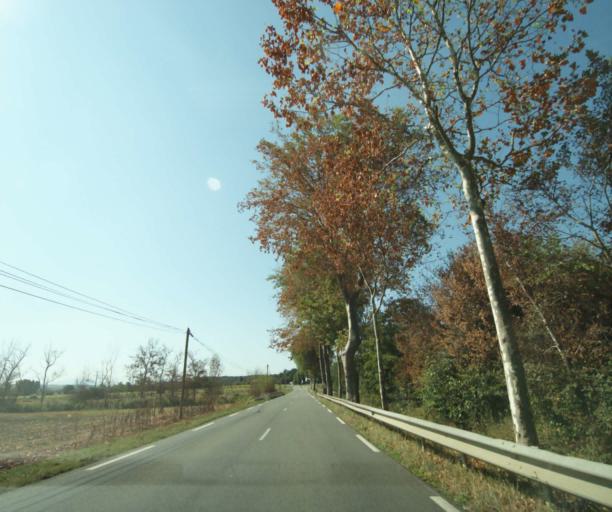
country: FR
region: Midi-Pyrenees
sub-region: Departement de la Haute-Garonne
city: Saint-Sulpice-sur-Leze
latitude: 43.3178
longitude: 1.3230
